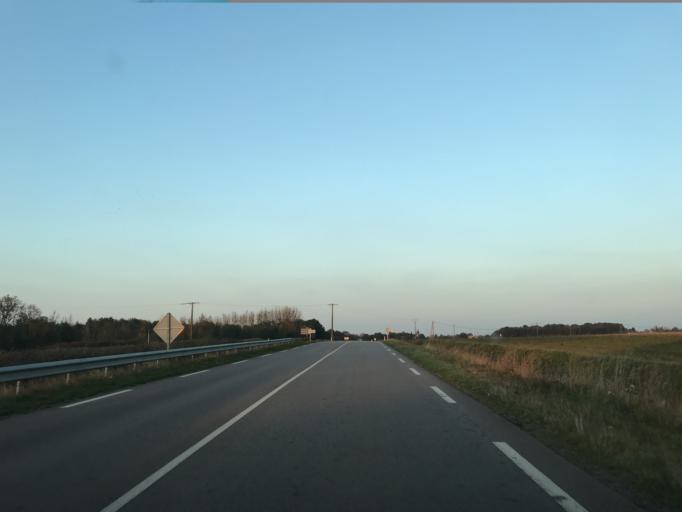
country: FR
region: Haute-Normandie
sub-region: Departement de l'Eure
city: Bourth
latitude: 48.6775
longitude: 0.7977
